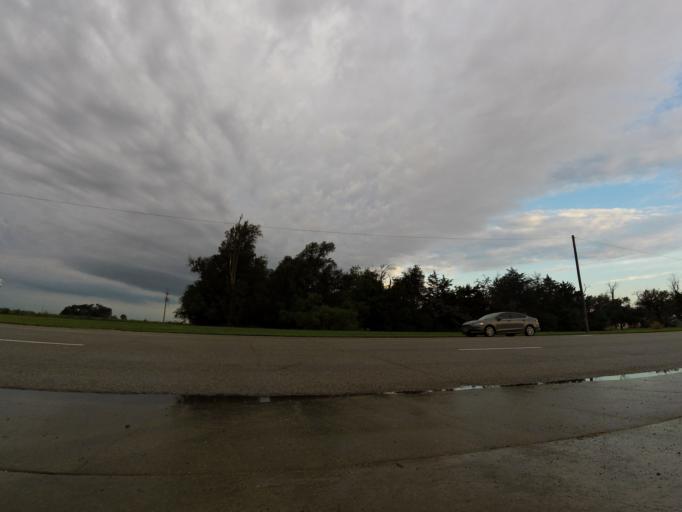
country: US
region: Kansas
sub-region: Reno County
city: South Hutchinson
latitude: 38.0153
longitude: -97.9400
